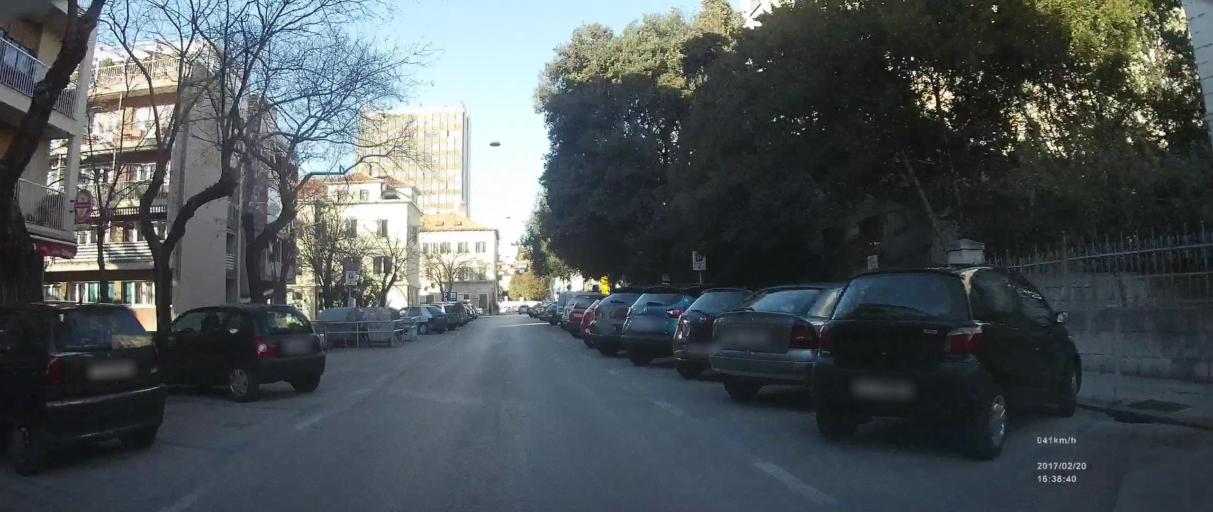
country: HR
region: Splitsko-Dalmatinska
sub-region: Grad Split
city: Split
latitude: 43.5044
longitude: 16.4455
